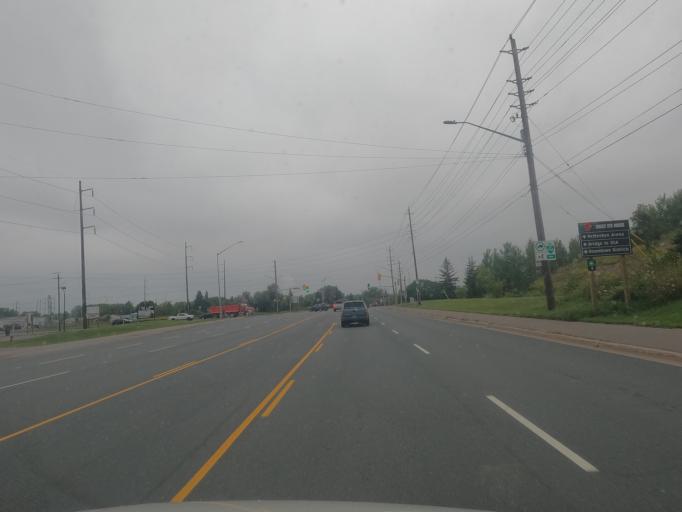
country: CA
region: Ontario
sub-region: Algoma
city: Sault Ste. Marie
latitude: 46.5385
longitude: -84.3446
